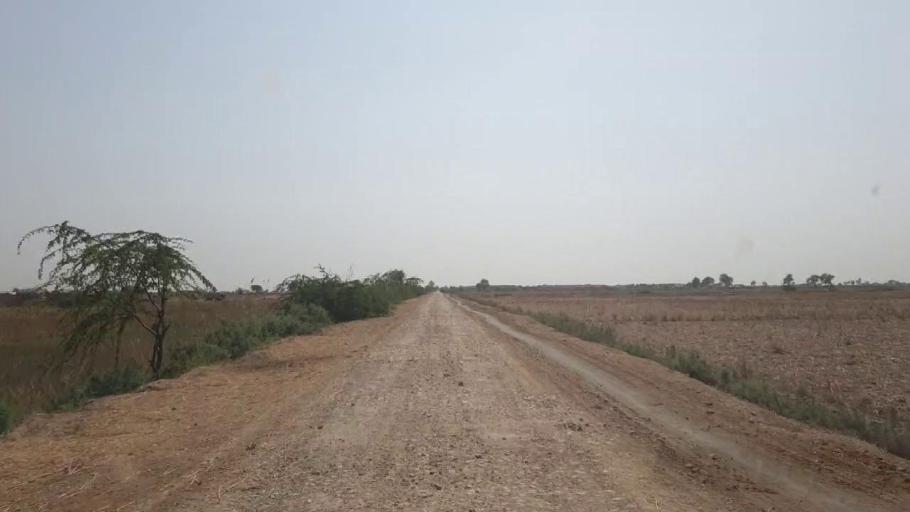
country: PK
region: Sindh
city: Jati
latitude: 24.4300
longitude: 68.5524
